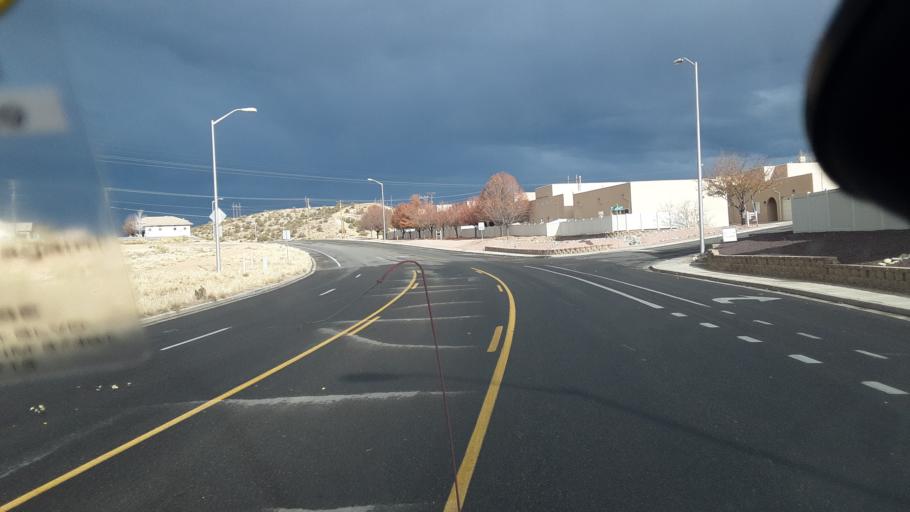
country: US
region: New Mexico
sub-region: San Juan County
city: Farmington
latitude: 36.7621
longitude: -108.1903
